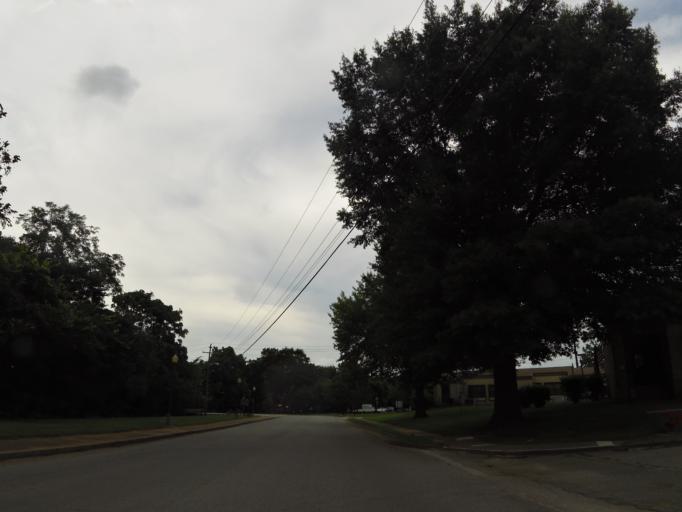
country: US
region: Kentucky
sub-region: Christian County
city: Hopkinsville
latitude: 36.8691
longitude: -87.4885
